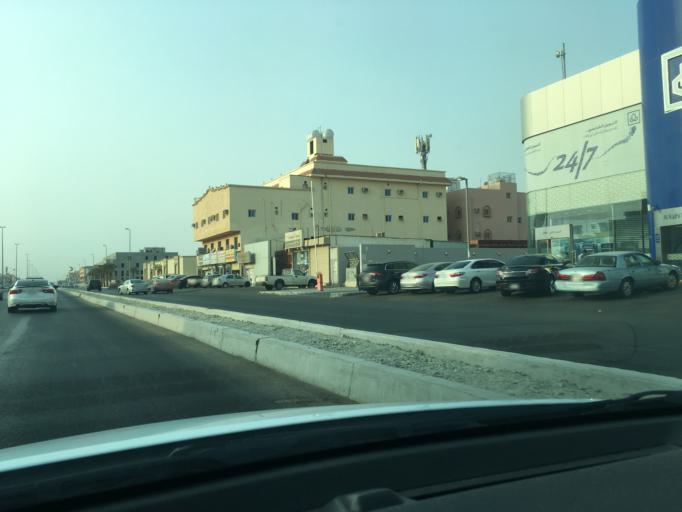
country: SA
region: Makkah
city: Jeddah
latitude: 21.7506
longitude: 39.1879
